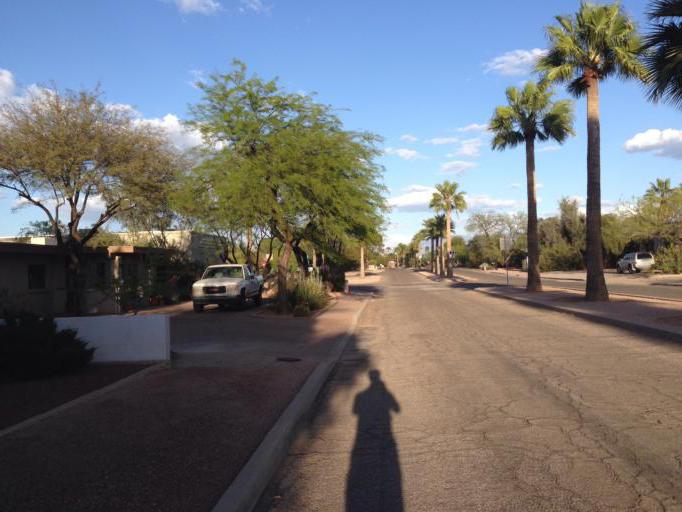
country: US
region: Arizona
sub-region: Pima County
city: Tucson
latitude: 32.2456
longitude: -110.9395
